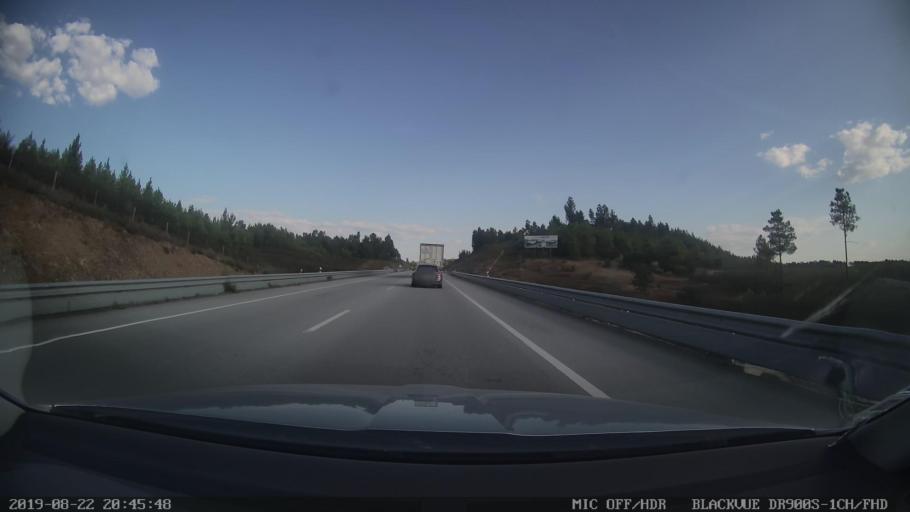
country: PT
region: Castelo Branco
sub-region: Proenca-A-Nova
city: Proenca-a-Nova
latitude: 39.7206
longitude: -7.8702
